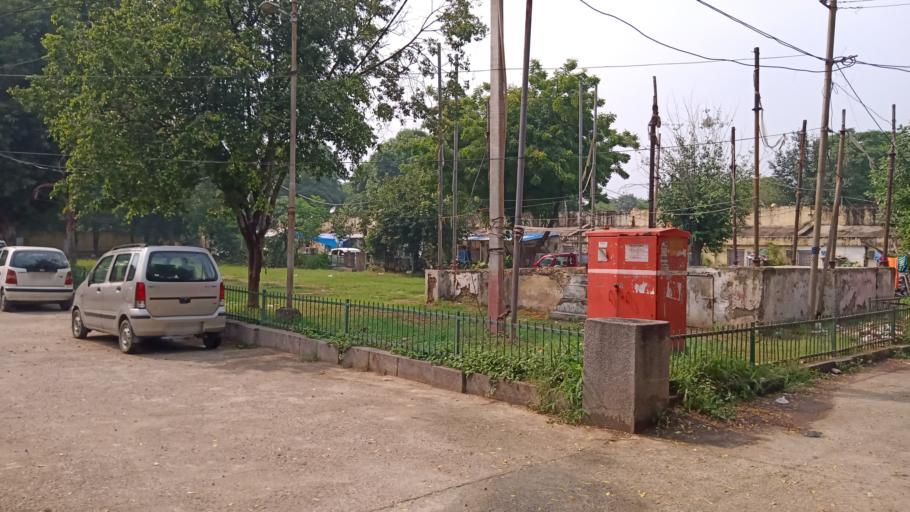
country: IN
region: NCT
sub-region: New Delhi
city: New Delhi
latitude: 28.5766
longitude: 77.2483
